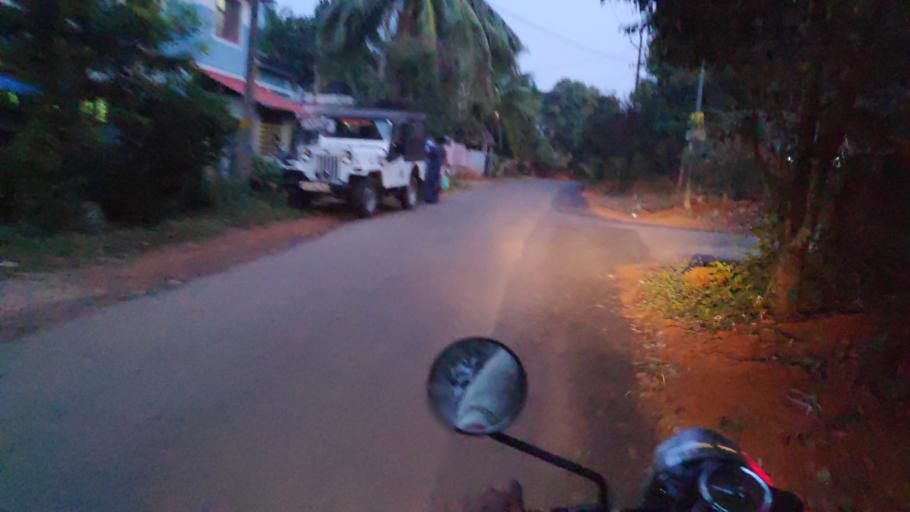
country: IN
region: Kerala
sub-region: Kozhikode
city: Kunnamangalam
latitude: 11.2807
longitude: 75.8320
